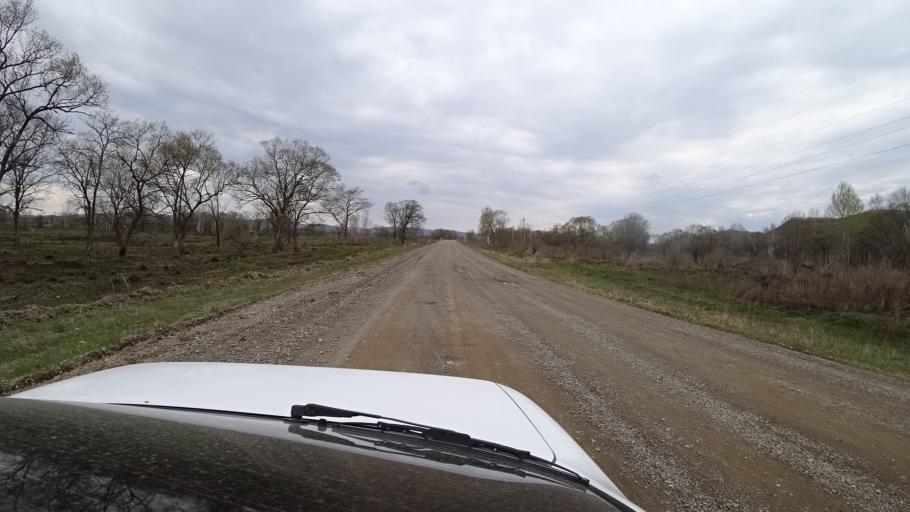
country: RU
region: Primorskiy
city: Novopokrovka
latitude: 45.5615
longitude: 134.3367
